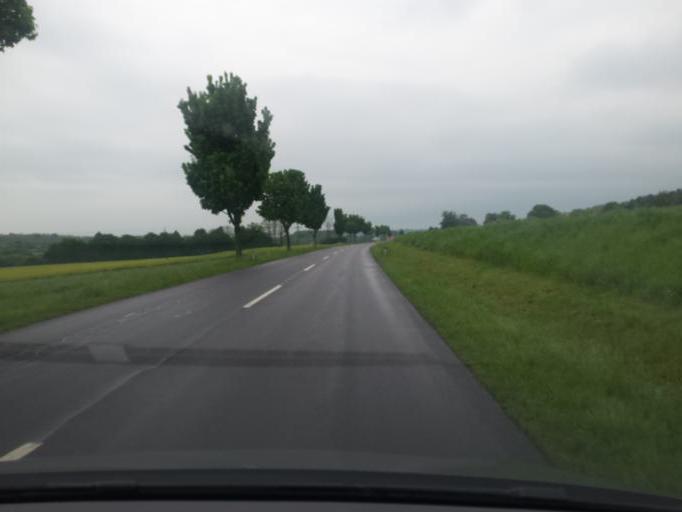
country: AT
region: Burgenland
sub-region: Politischer Bezirk Oberpullendorf
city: Mannersdorf an der Rabnitz
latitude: 47.4705
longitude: 16.5595
